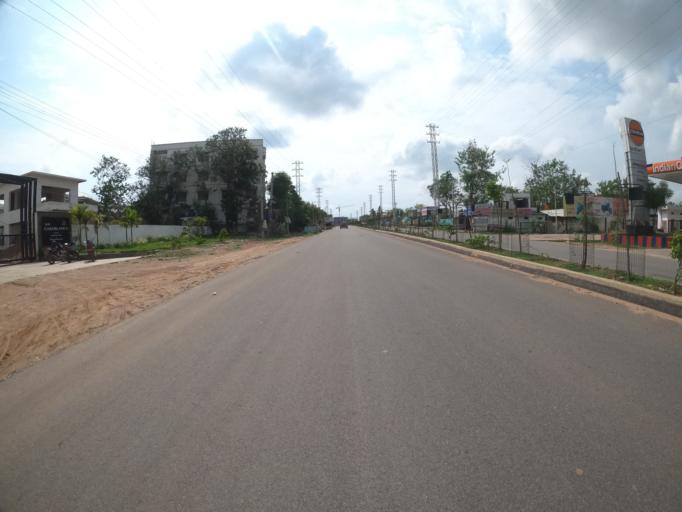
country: IN
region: Telangana
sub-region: Medak
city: Serilingampalle
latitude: 17.3878
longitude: 78.3284
